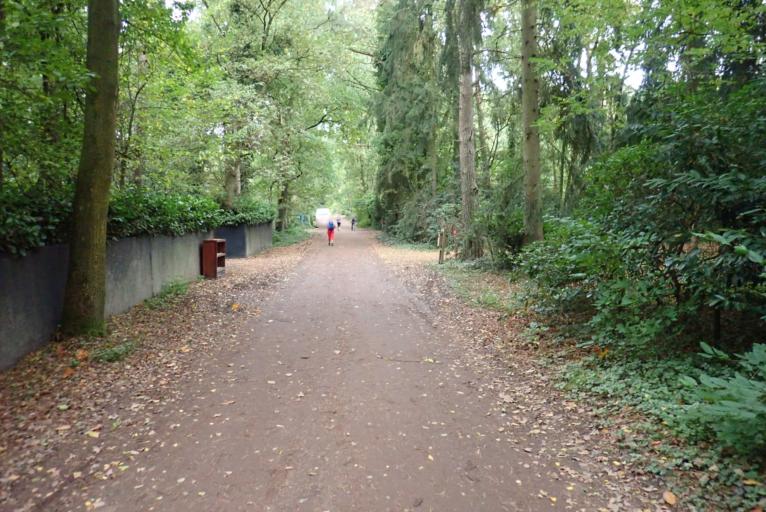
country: BE
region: Flanders
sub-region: Provincie Antwerpen
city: Essen
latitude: 51.4322
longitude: 4.4446
